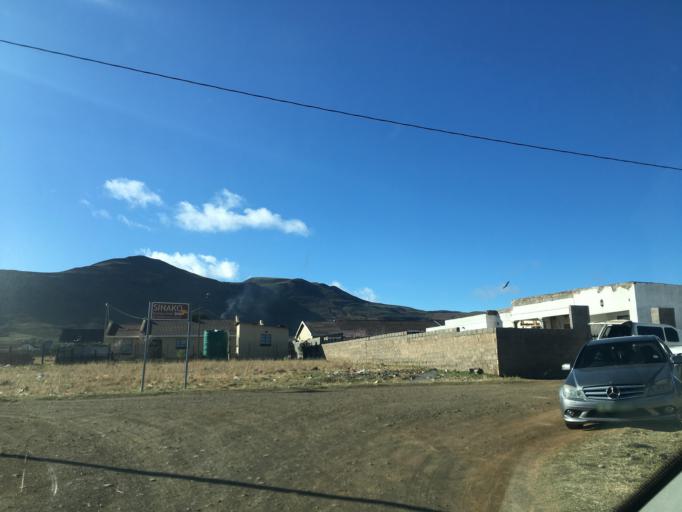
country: ZA
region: Eastern Cape
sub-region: Chris Hani District Municipality
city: Cala
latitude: -31.5383
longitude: 27.6951
